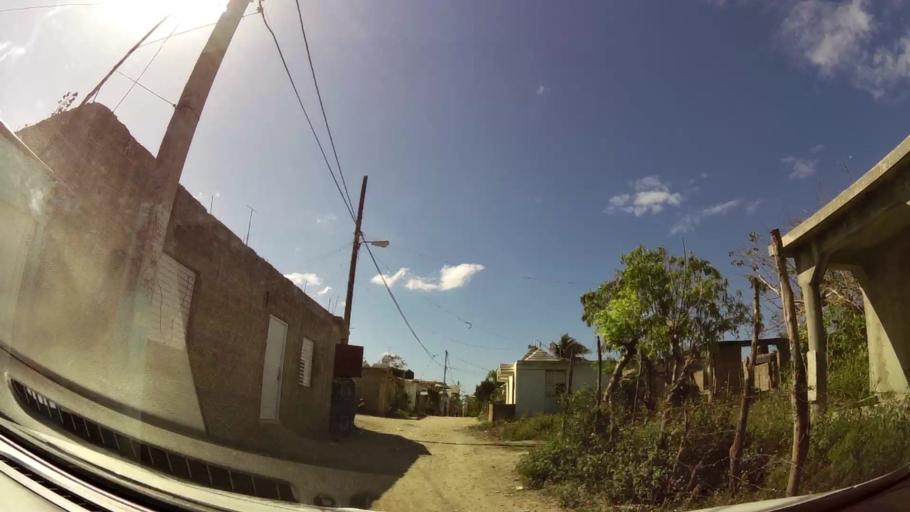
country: DO
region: Santo Domingo
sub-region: Santo Domingo
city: Boca Chica
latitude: 18.4625
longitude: -69.6116
